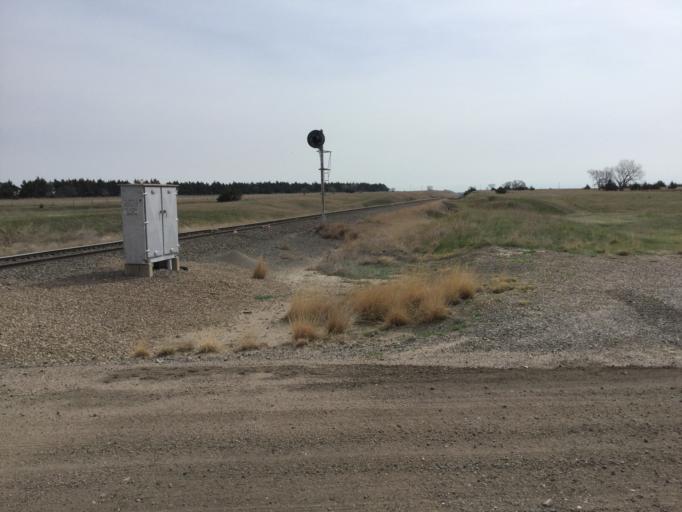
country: US
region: Kansas
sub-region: Norton County
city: Norton
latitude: 39.8177
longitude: -99.9438
